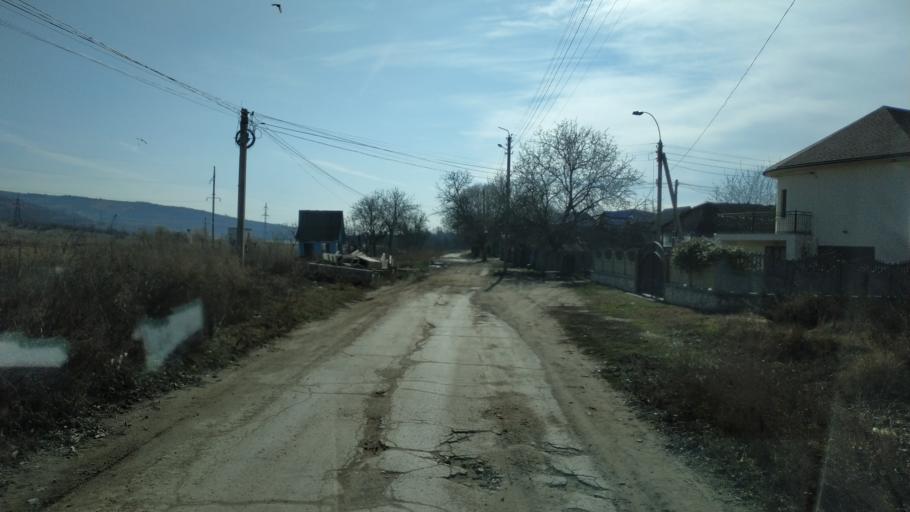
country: MD
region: Nisporeni
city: Nisporeni
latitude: 47.0643
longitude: 28.1725
